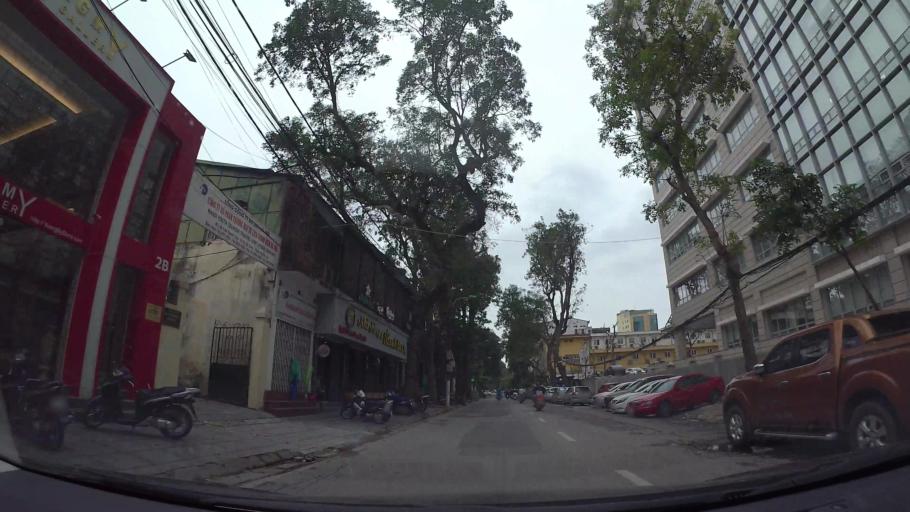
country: VN
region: Ha Noi
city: Hai BaTrung
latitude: 21.0166
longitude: 105.8593
